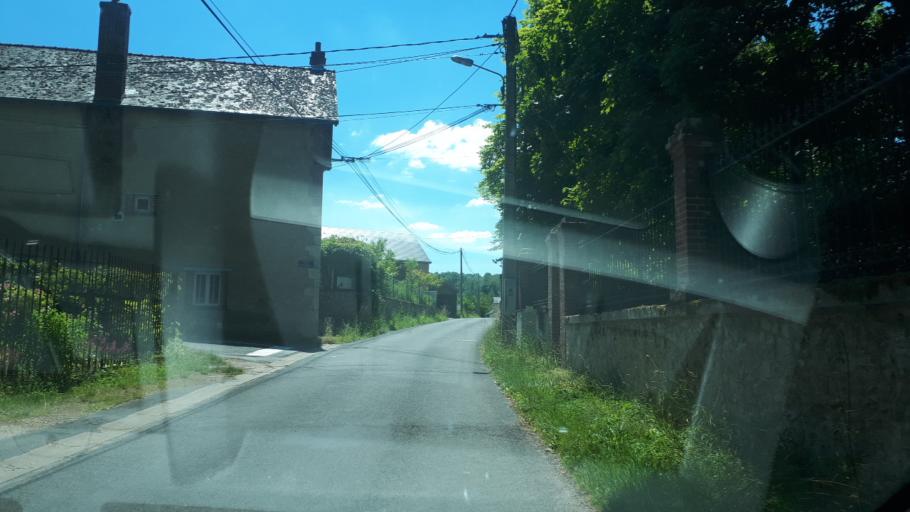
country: FR
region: Centre
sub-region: Departement du Loir-et-Cher
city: Saint-Sulpice-de-Pommeray
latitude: 47.5916
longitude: 1.2088
